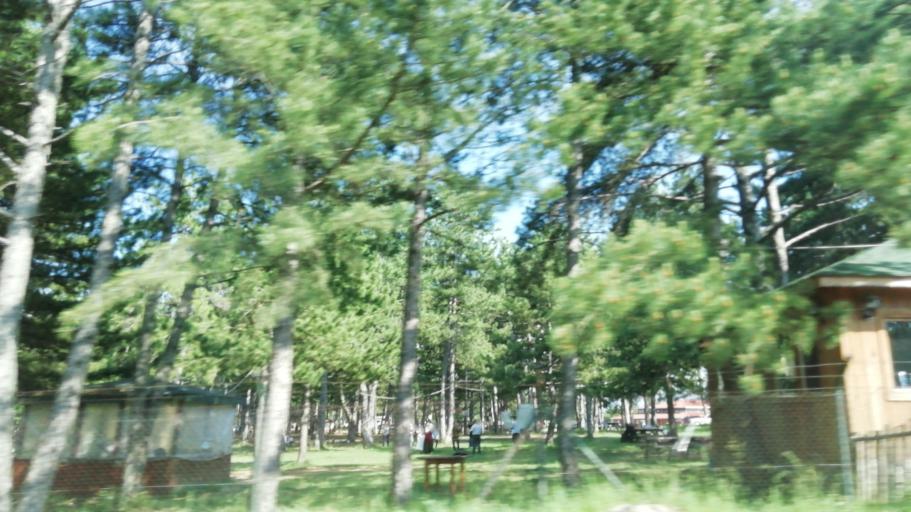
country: TR
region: Karabuk
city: Karabuk
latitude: 41.1079
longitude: 32.6046
